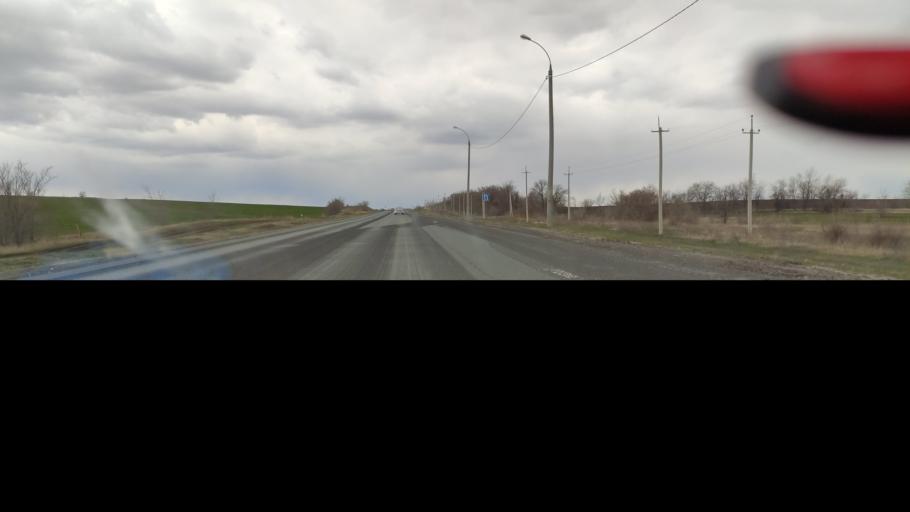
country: RU
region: Saratov
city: Shumeyka
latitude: 51.7860
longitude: 46.1375
